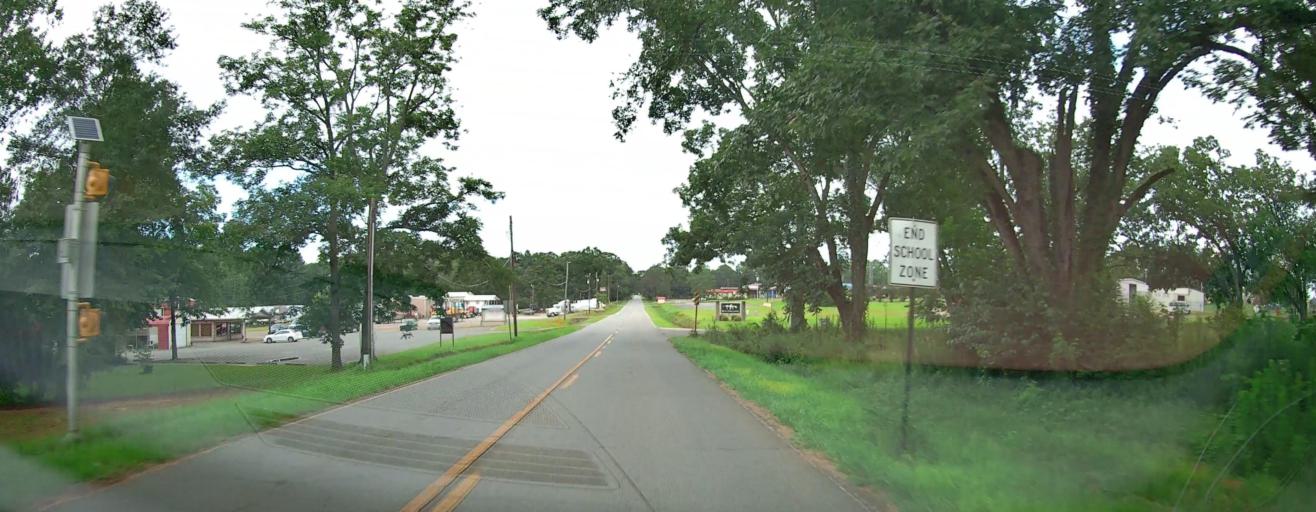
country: US
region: Georgia
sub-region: Schley County
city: Ellaville
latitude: 32.2204
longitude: -84.2941
